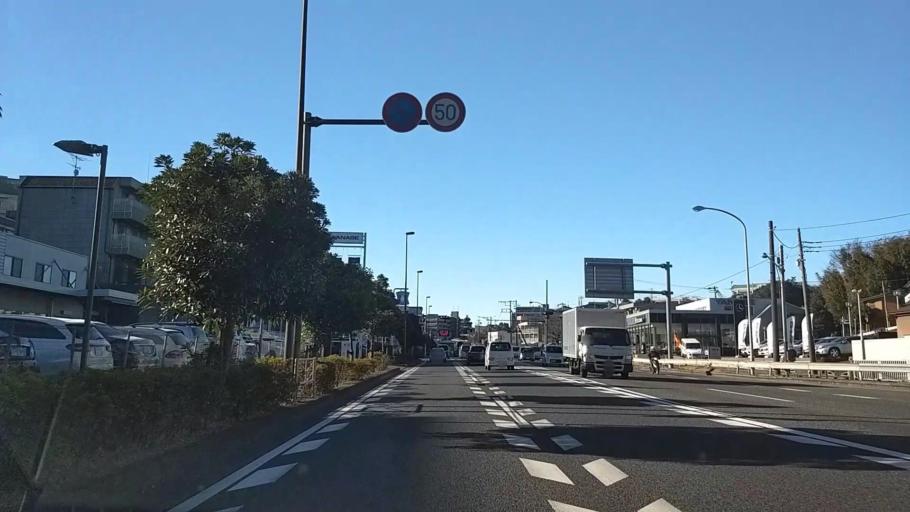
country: JP
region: Kanagawa
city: Yokohama
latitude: 35.4744
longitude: 139.5997
